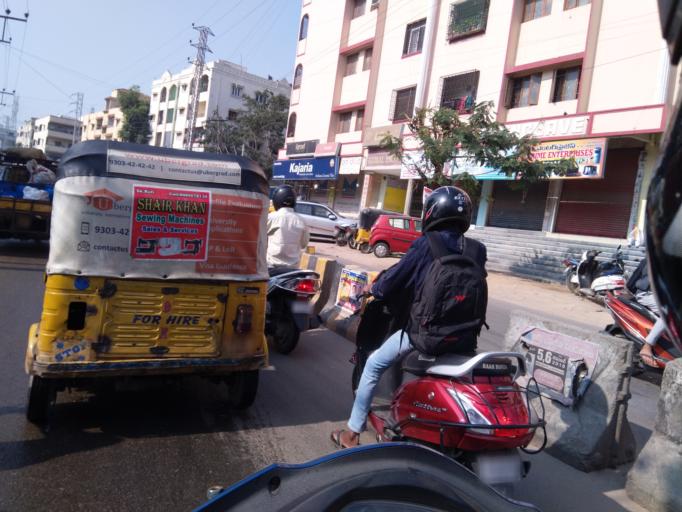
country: IN
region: Telangana
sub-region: Rangareddi
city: Kukatpalli
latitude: 17.4960
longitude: 78.4058
